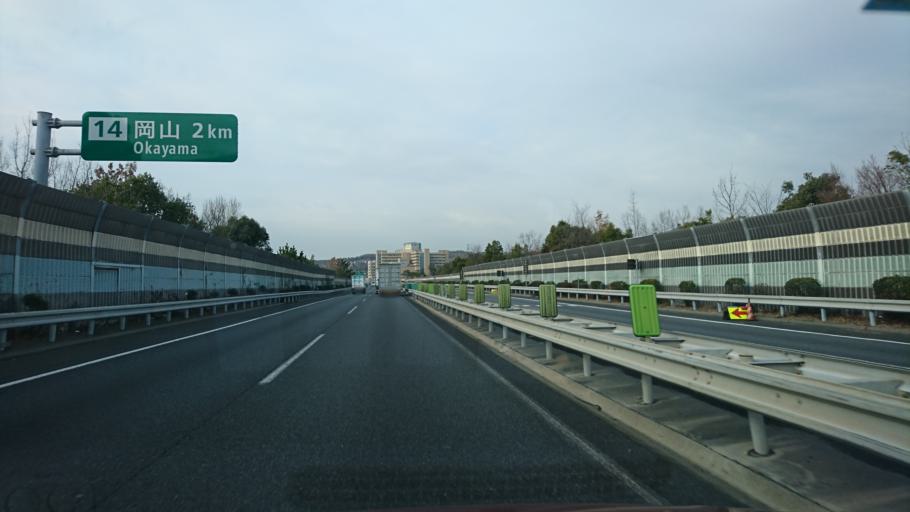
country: JP
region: Okayama
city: Okayama-shi
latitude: 34.7087
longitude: 133.9078
